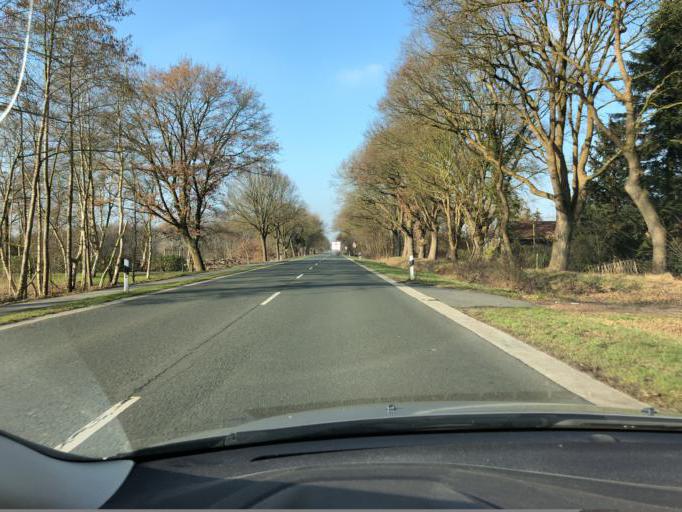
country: DE
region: Lower Saxony
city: Westerstede
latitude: 53.2937
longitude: 7.8537
